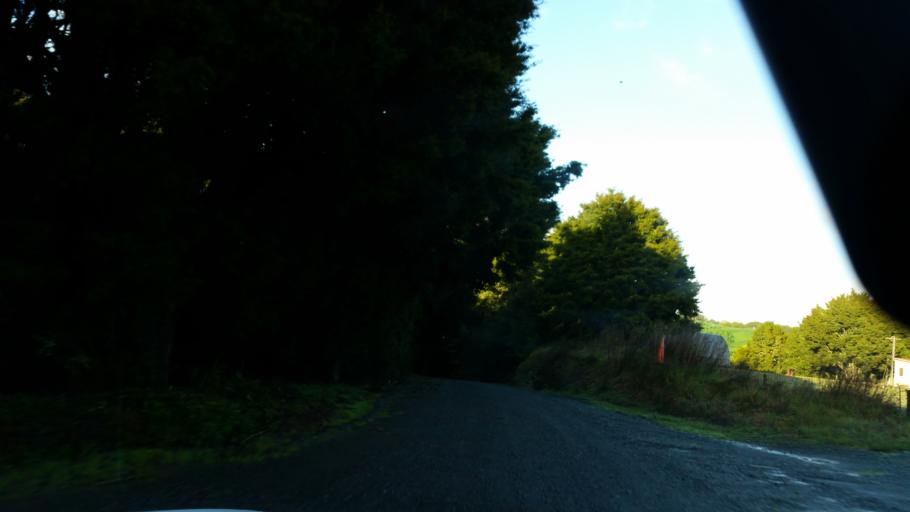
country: NZ
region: Northland
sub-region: Whangarei
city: Maungatapere
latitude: -35.7765
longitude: 174.1081
